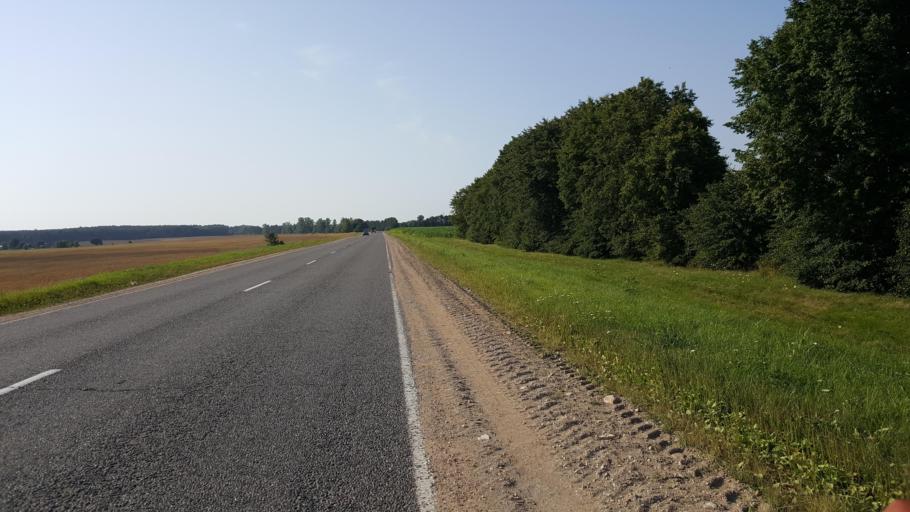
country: BY
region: Brest
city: Kamyanyets
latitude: 52.3643
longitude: 23.8890
